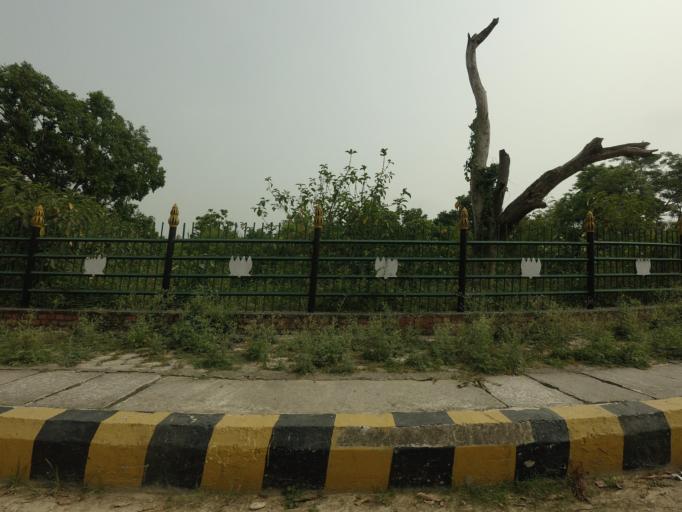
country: IN
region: Uttar Pradesh
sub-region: Maharajganj
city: Nautanwa
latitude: 27.4625
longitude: 83.2827
